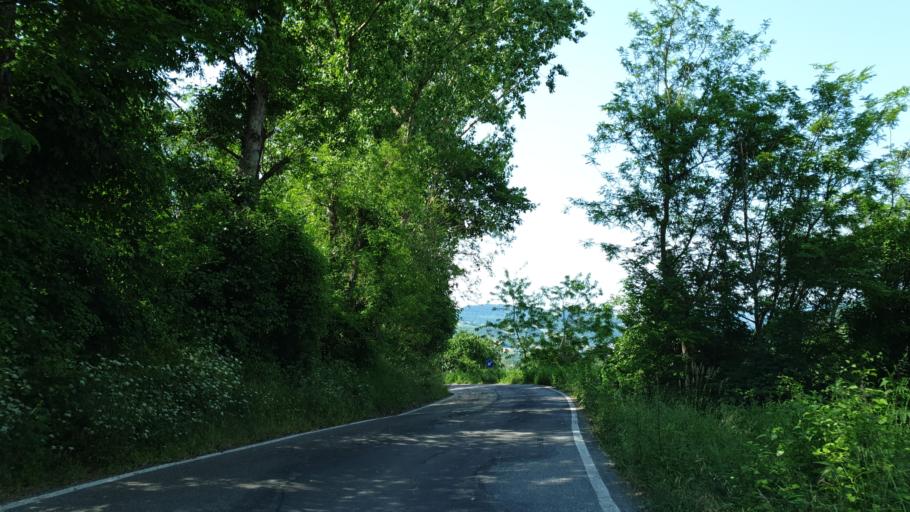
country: IT
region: Emilia-Romagna
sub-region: Forli-Cesena
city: Sarsina
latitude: 43.9121
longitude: 12.1752
